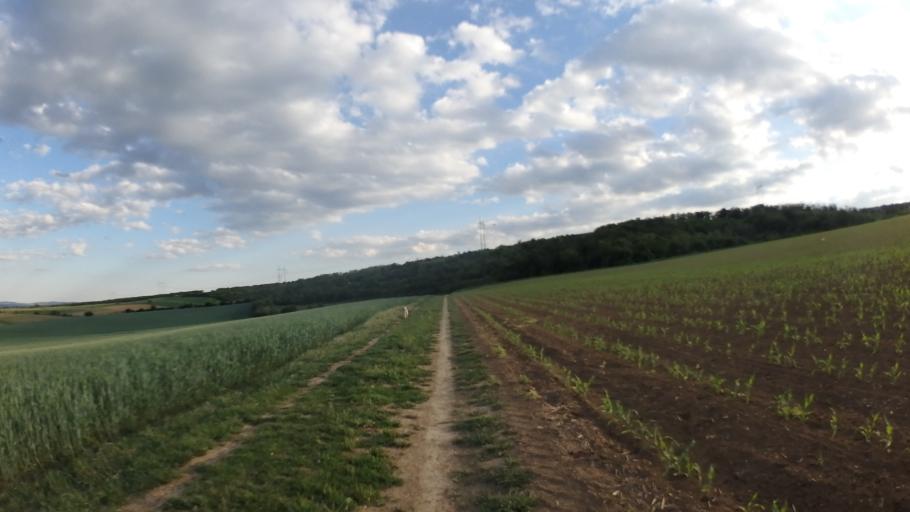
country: CZ
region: South Moravian
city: Moravany
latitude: 49.1343
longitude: 16.5888
